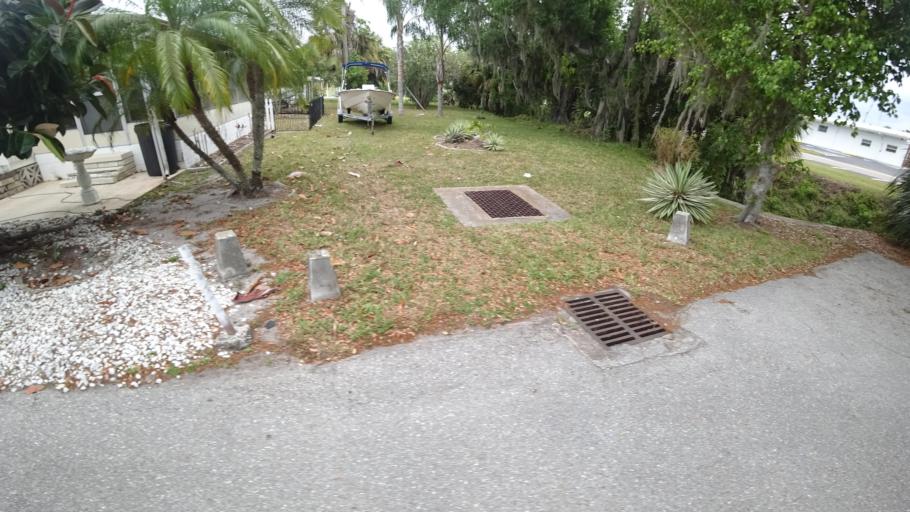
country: US
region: Florida
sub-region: Manatee County
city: West Samoset
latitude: 27.4500
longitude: -82.5632
